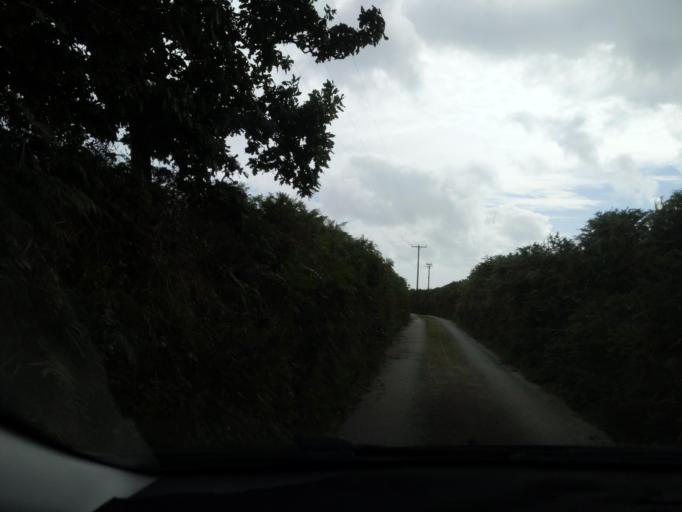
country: GB
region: England
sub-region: Cornwall
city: Par
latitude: 50.3855
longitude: -4.7022
